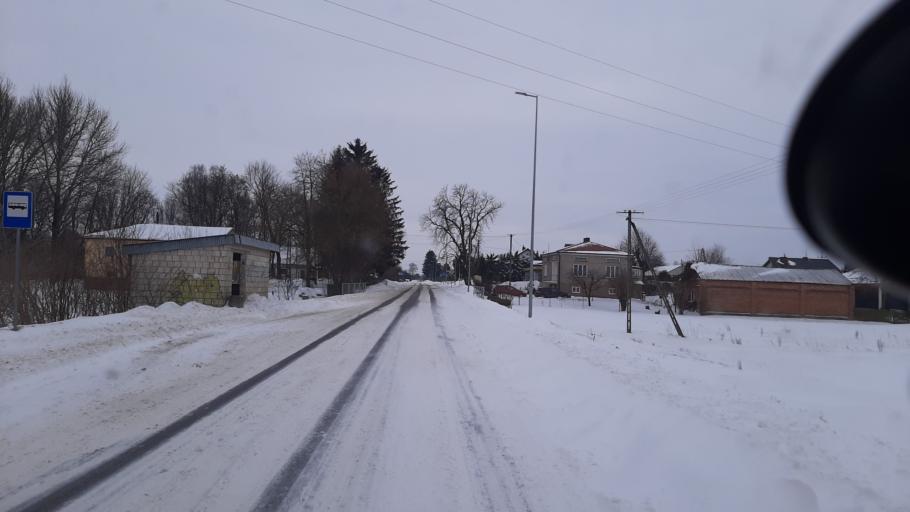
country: PL
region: Lublin Voivodeship
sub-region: Powiat lubelski
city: Garbow
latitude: 51.3203
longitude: 22.3188
